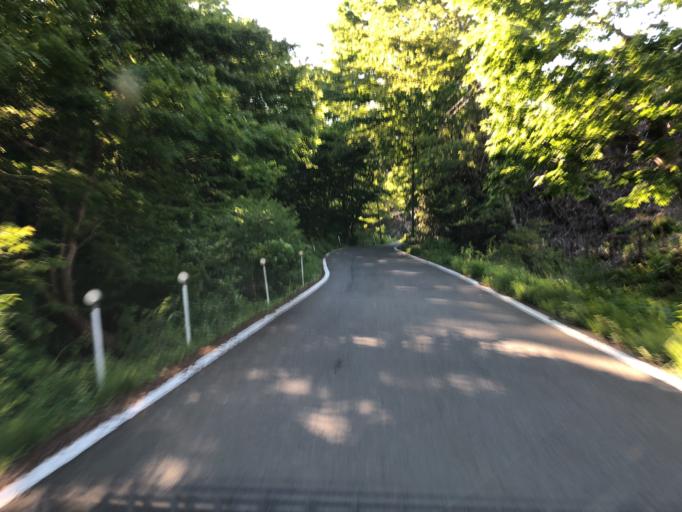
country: JP
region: Ibaraki
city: Kitaibaraki
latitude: 36.8970
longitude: 140.5980
